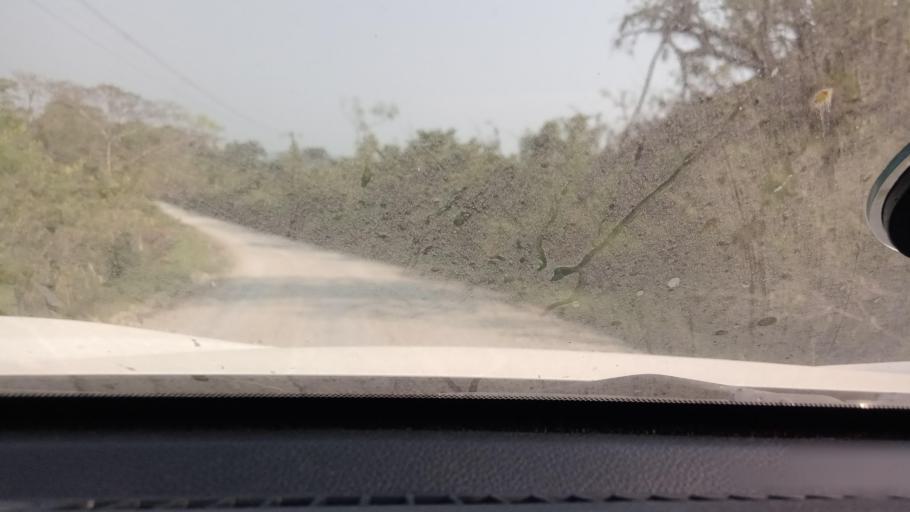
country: MX
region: Tabasco
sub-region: Huimanguillo
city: Francisco Rueda
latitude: 17.6148
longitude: -93.9391
